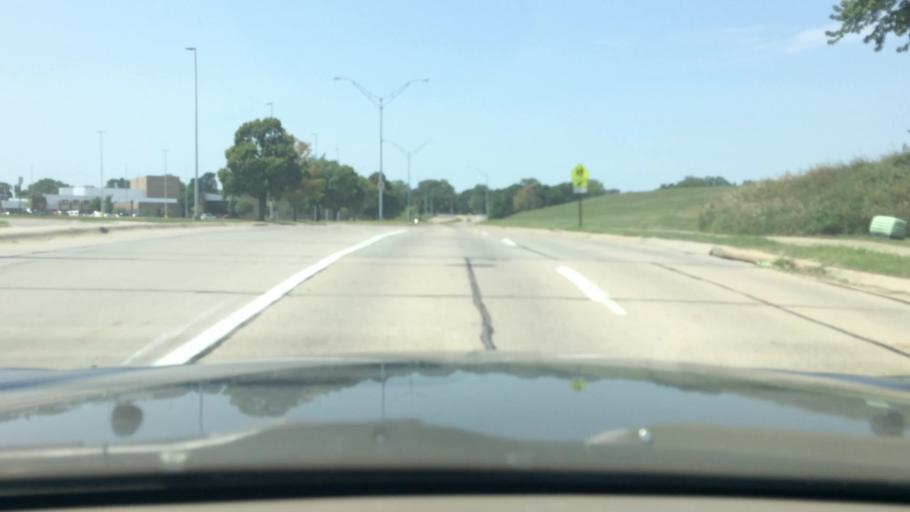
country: US
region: Nebraska
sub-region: Douglas County
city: Ralston
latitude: 41.2015
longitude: -96.0475
